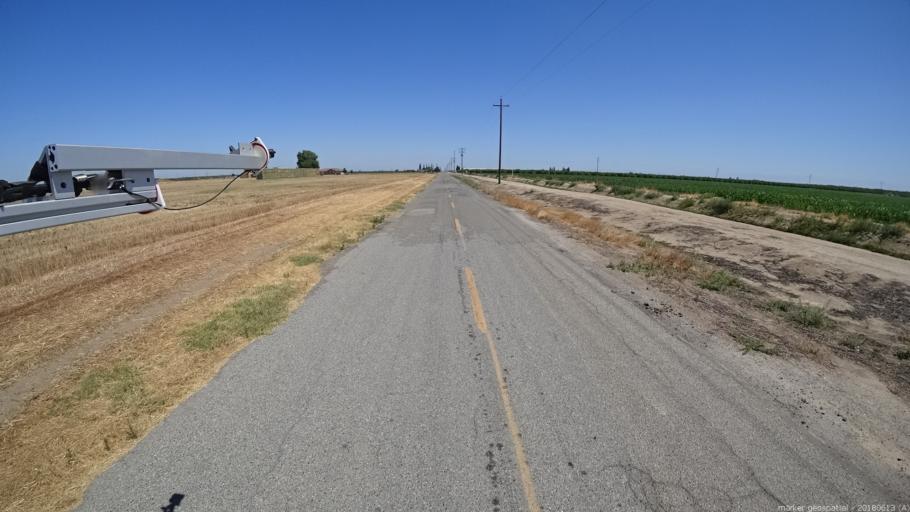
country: US
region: California
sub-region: Madera County
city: Chowchilla
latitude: 37.0551
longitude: -120.3469
